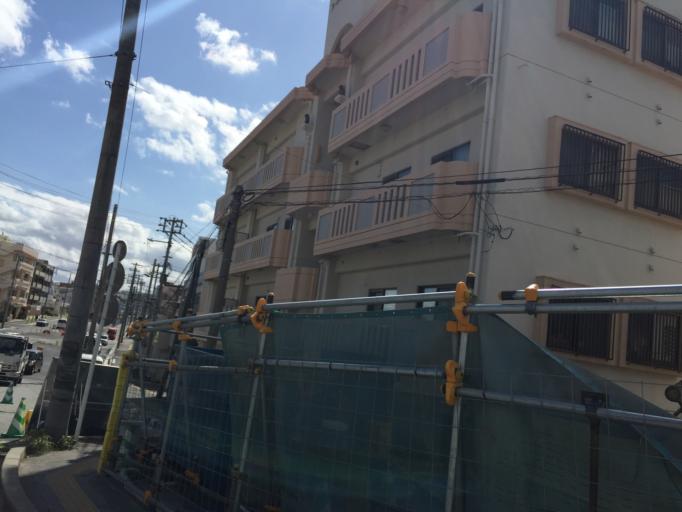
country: JP
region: Okinawa
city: Ginowan
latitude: 26.2341
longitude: 127.7285
